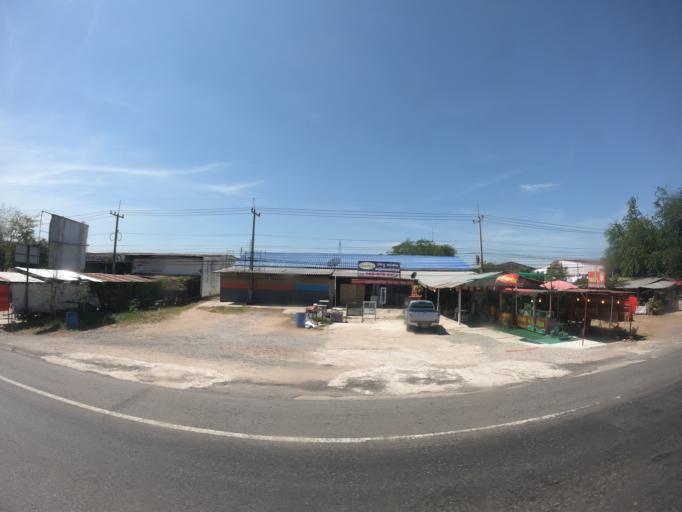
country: TH
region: Khon Kaen
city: Phon
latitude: 15.8048
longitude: 102.6073
